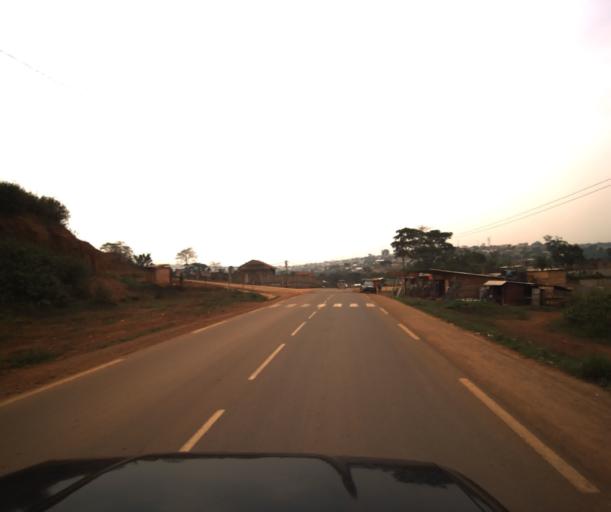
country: CM
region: Centre
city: Yaounde
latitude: 3.8074
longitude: 11.4639
